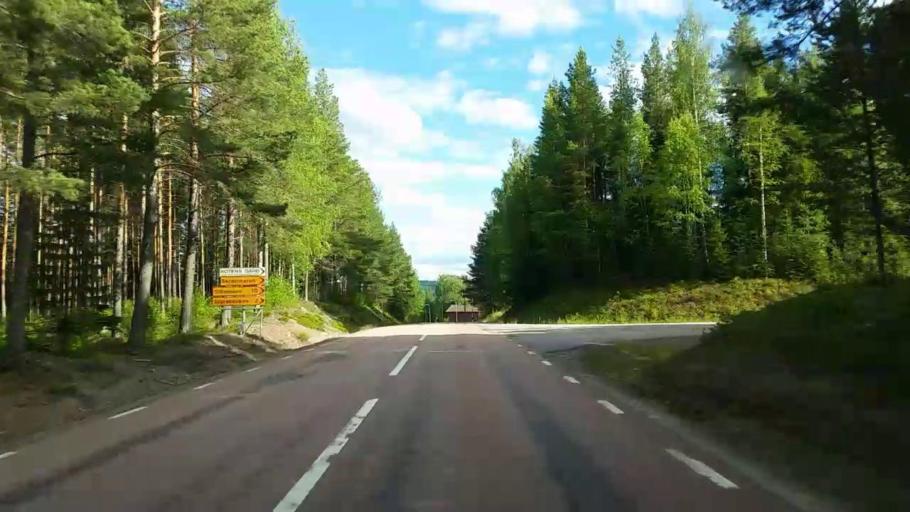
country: SE
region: Gaevleborg
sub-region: Ljusdals Kommun
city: Farila
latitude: 61.9111
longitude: 15.8859
